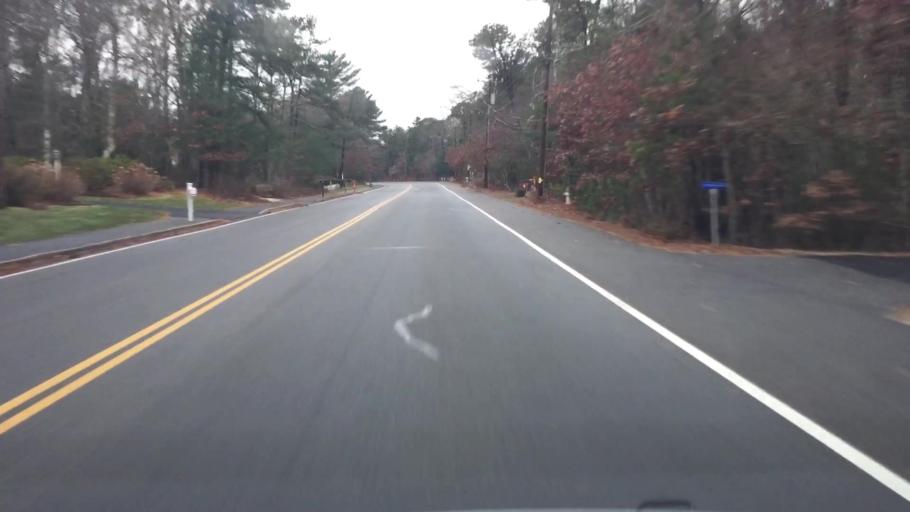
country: US
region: Massachusetts
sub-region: Barnstable County
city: North Falmouth
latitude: 41.6356
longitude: -70.6269
